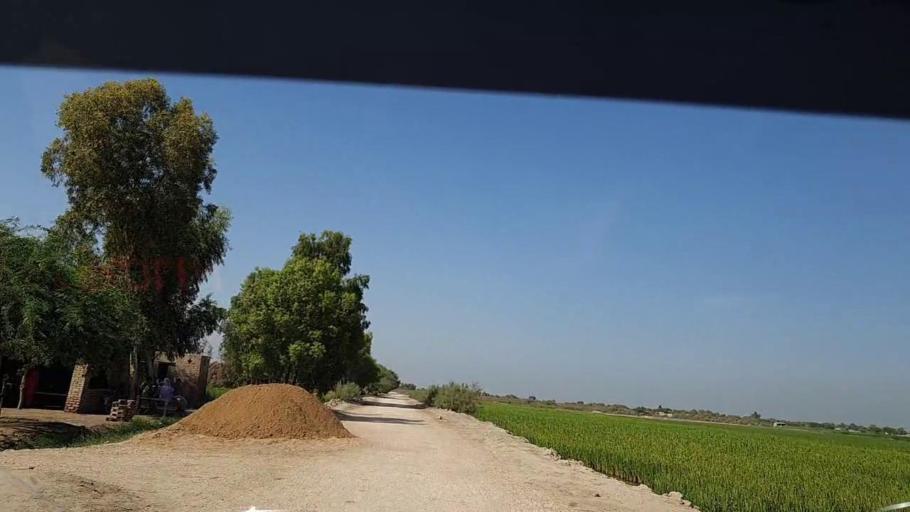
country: PK
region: Sindh
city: Tangwani
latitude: 28.3325
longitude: 69.0725
